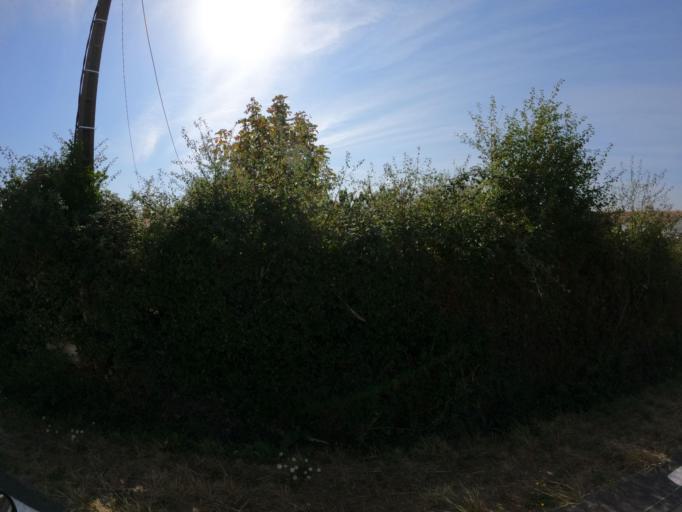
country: FR
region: Pays de la Loire
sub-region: Departement de la Vendee
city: Saint-Christophe-du-Ligneron
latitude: 46.8167
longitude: -1.7680
